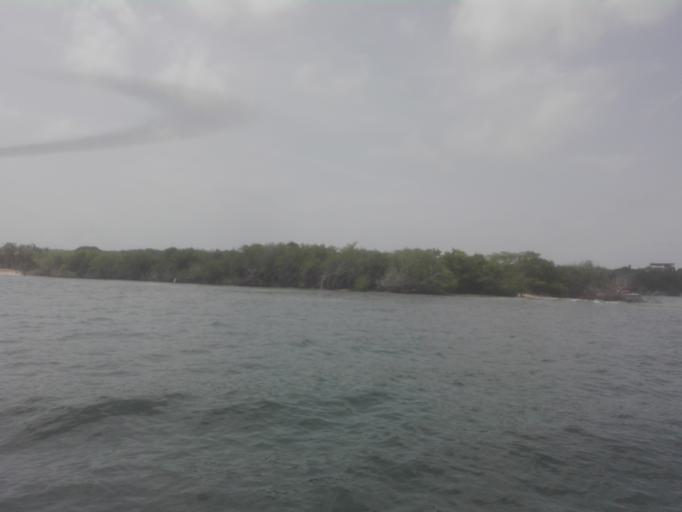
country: CO
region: Bolivar
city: Turbana
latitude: 10.1558
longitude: -75.6878
